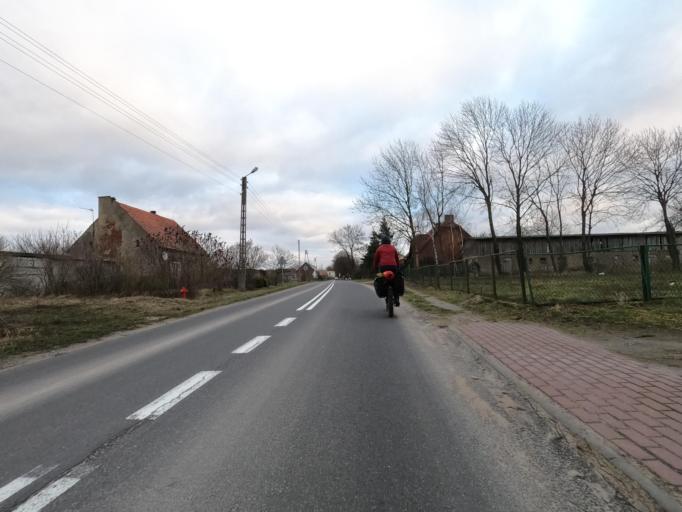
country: PL
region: Greater Poland Voivodeship
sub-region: Powiat pilski
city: Bialosliwie
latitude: 53.1102
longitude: 17.1900
